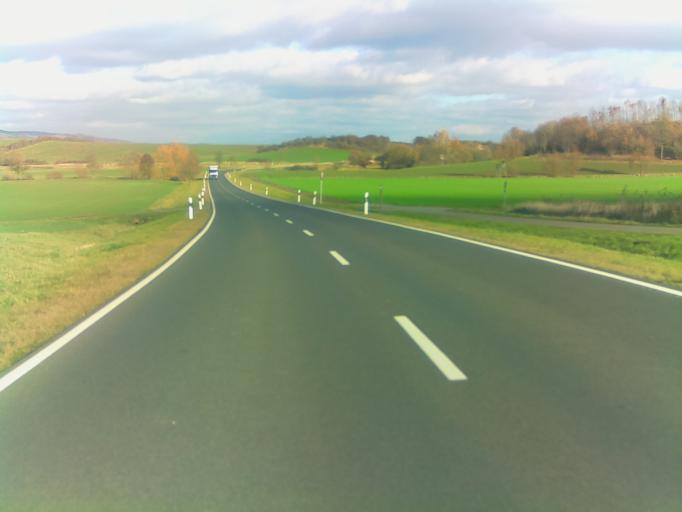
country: DE
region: Bavaria
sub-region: Regierungsbezirk Unterfranken
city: Trappstadt
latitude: 50.3289
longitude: 10.5792
